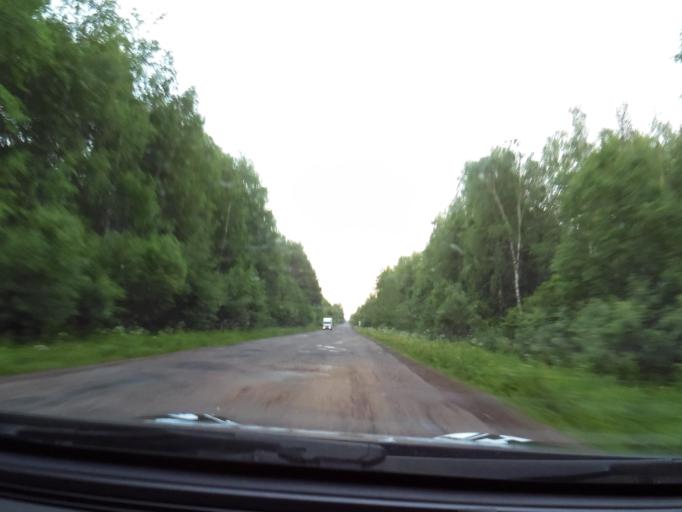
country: RU
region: Leningrad
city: Voznesen'ye
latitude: 60.8335
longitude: 35.6756
